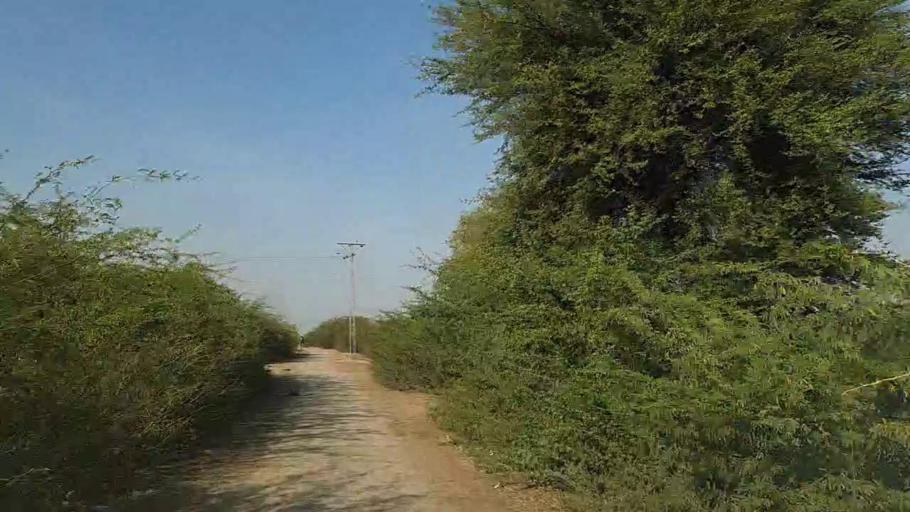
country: PK
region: Sindh
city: Naukot
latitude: 24.9351
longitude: 69.4591
